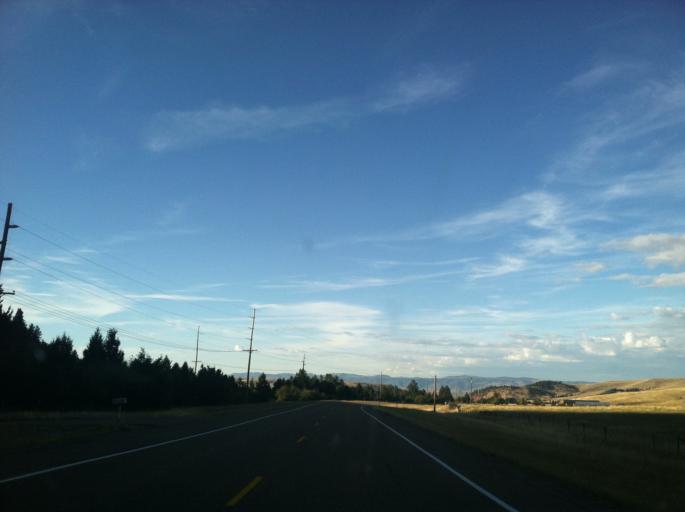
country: US
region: Montana
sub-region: Granite County
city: Philipsburg
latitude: 46.4797
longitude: -113.2347
